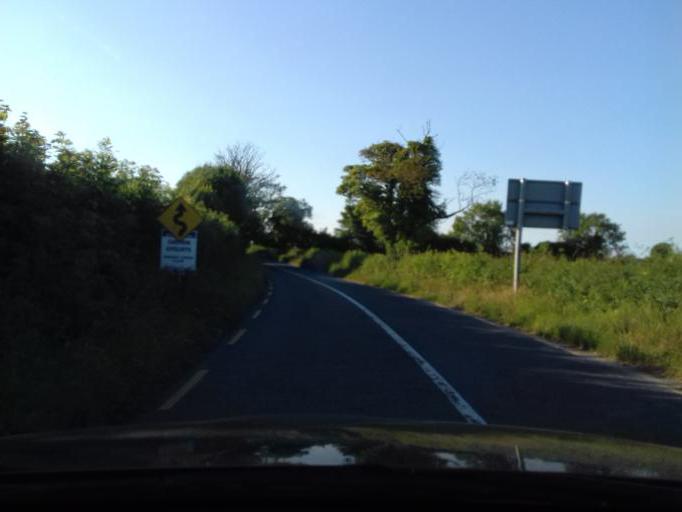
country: IE
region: Leinster
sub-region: An Mhi
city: Ashbourne
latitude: 53.5398
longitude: -6.3684
